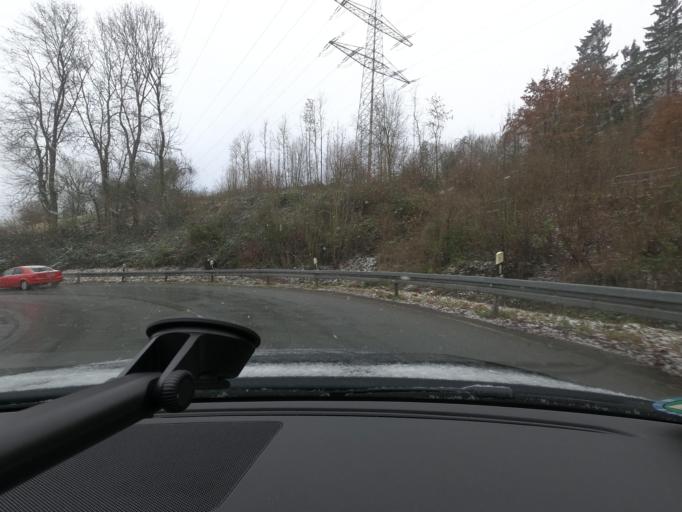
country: DE
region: North Rhine-Westphalia
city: Marsberg
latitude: 51.5025
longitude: 8.8678
